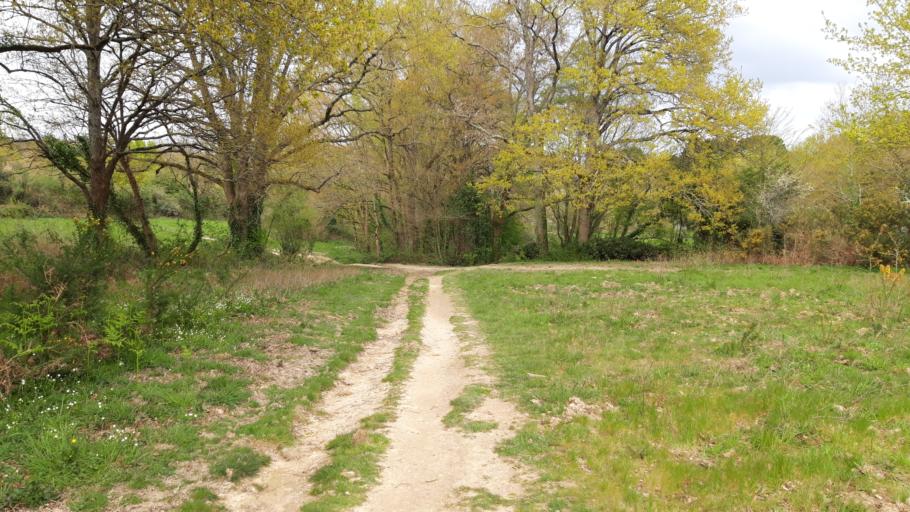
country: FR
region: Pays de la Loire
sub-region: Departement de la Loire-Atlantique
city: Orvault
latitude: 47.2335
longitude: -1.6075
